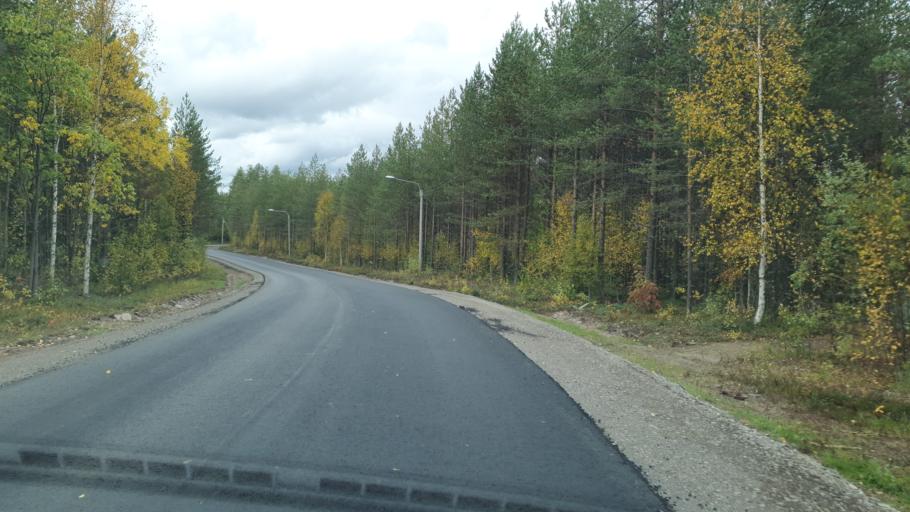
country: FI
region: Lapland
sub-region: Rovaniemi
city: Rovaniemi
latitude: 66.4238
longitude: 25.4022
